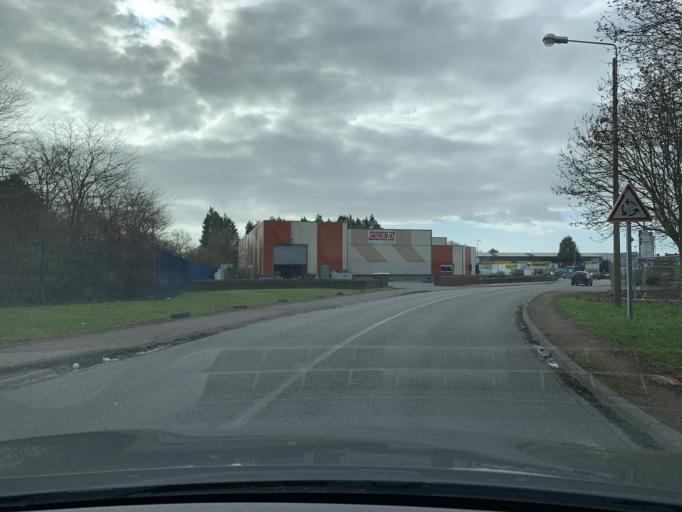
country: FR
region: Nord-Pas-de-Calais
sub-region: Departement du Nord
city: Waziers
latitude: 50.3926
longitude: 3.1056
